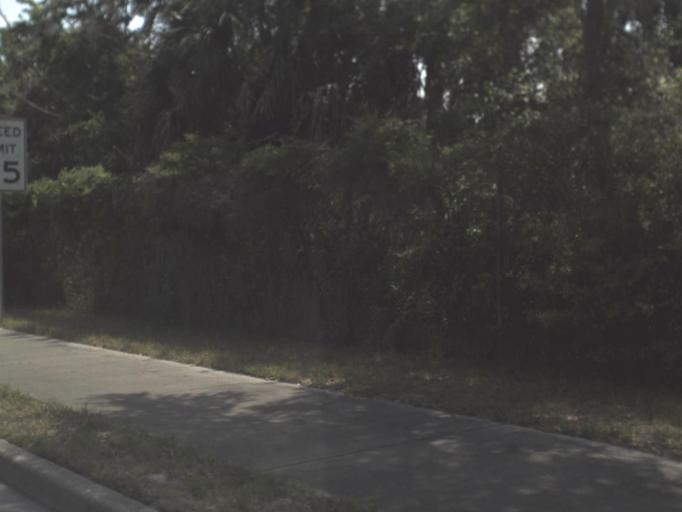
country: US
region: Florida
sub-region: Duval County
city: Atlantic Beach
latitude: 30.3728
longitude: -81.4103
